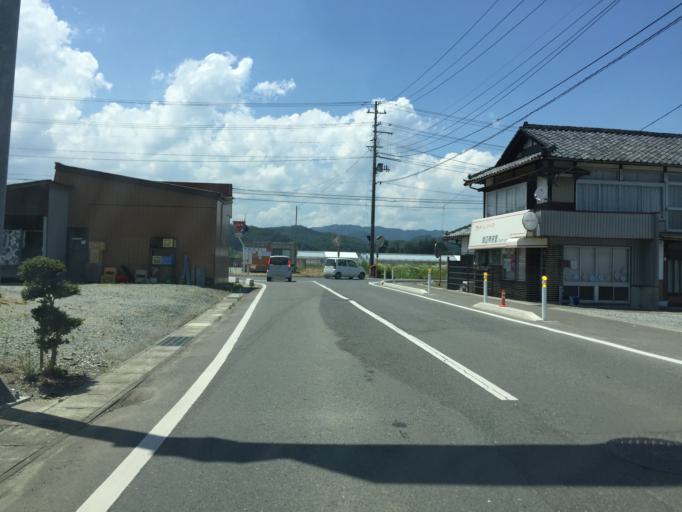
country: JP
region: Fukushima
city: Namie
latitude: 37.7198
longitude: 140.9300
